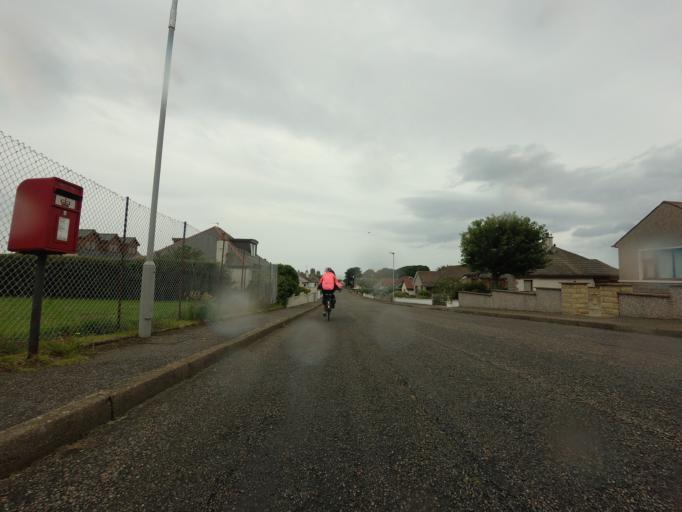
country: GB
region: Scotland
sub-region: Moray
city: Cullen
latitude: 57.6870
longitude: -2.8178
